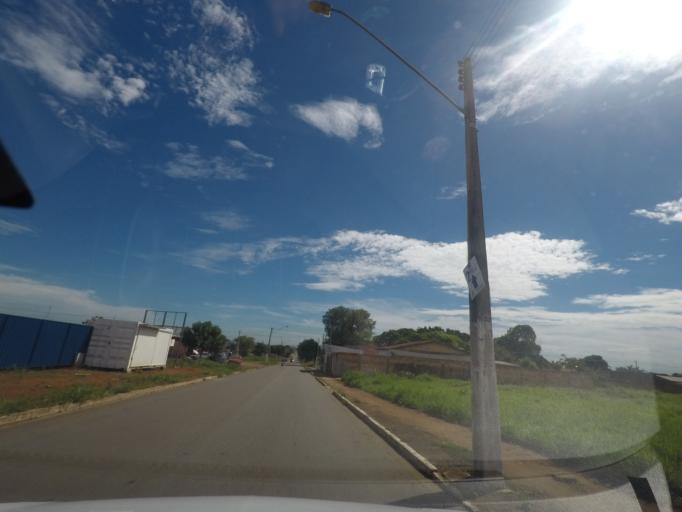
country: BR
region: Goias
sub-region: Aparecida De Goiania
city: Aparecida de Goiania
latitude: -16.8183
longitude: -49.2932
